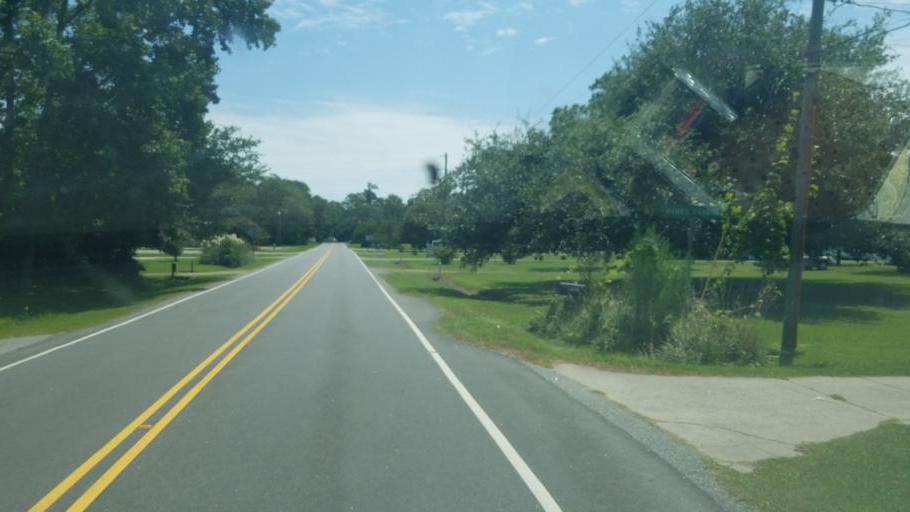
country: US
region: North Carolina
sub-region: Dare County
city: Manteo
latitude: 35.8930
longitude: -75.7694
